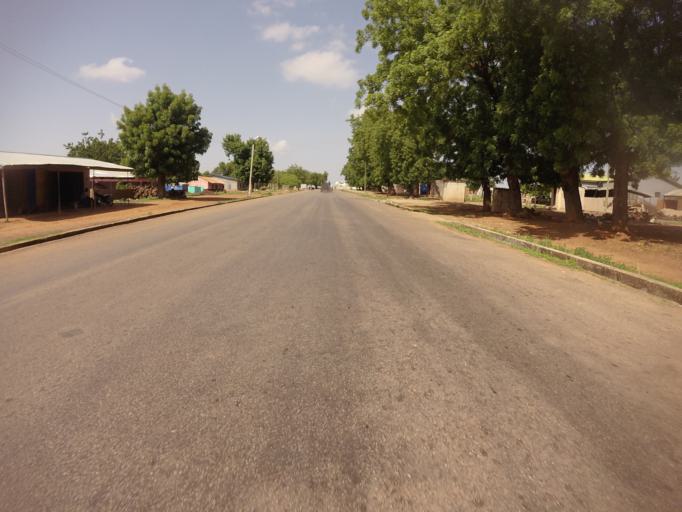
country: GH
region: Upper East
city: Bawku
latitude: 11.0697
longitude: -0.2064
